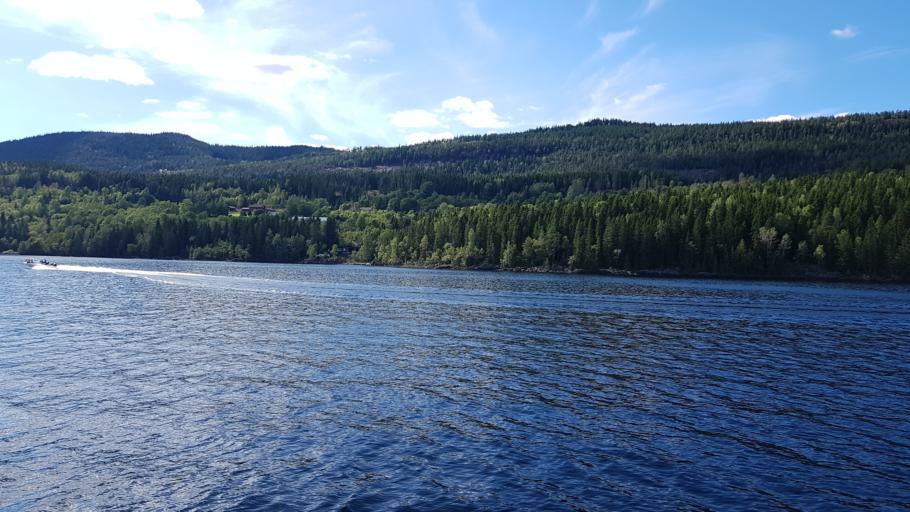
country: NO
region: Akershus
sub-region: Hurdal
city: Hurdal
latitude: 60.5412
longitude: 11.1990
